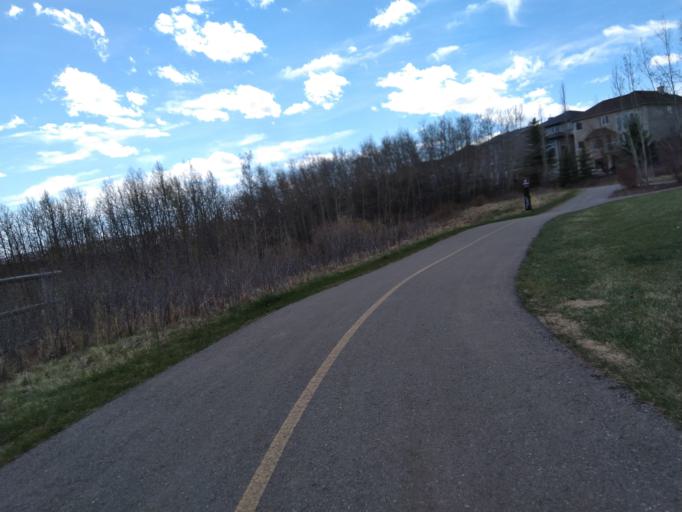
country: CA
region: Alberta
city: Calgary
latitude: 51.1197
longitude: -114.2368
